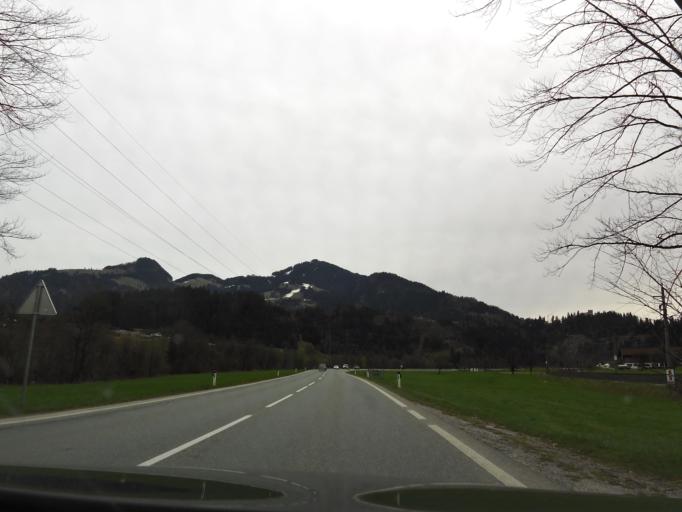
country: AT
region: Tyrol
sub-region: Politischer Bezirk Kitzbuhel
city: Itter
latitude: 47.4805
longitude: 12.1273
